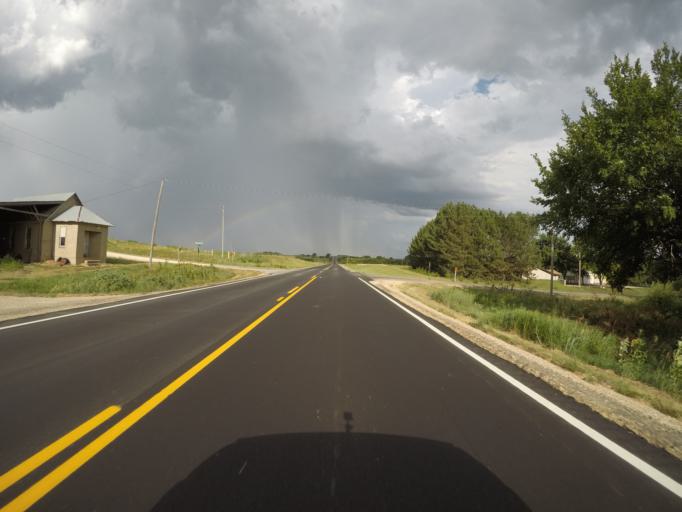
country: US
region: Kansas
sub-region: Marshall County
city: Blue Rapids
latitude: 39.4365
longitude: -96.7929
